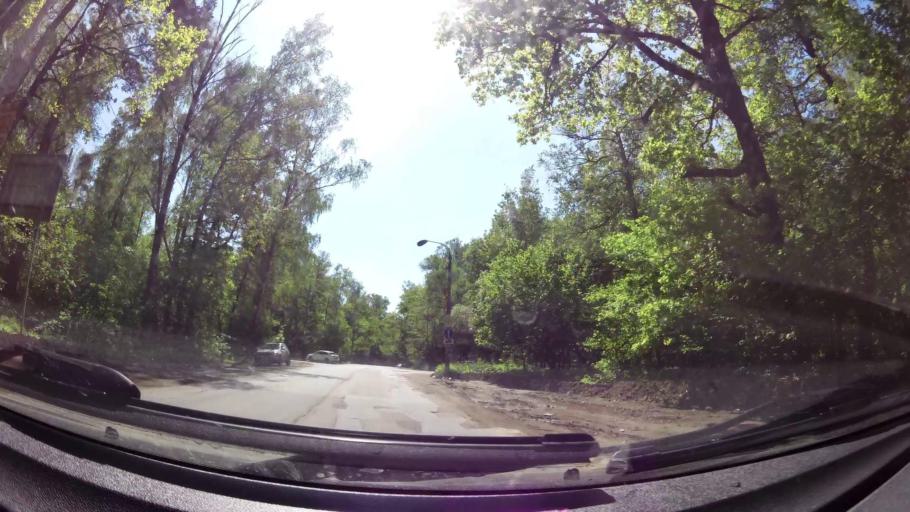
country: RU
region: Moscow
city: Lianozovo
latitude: 55.9229
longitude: 37.5974
